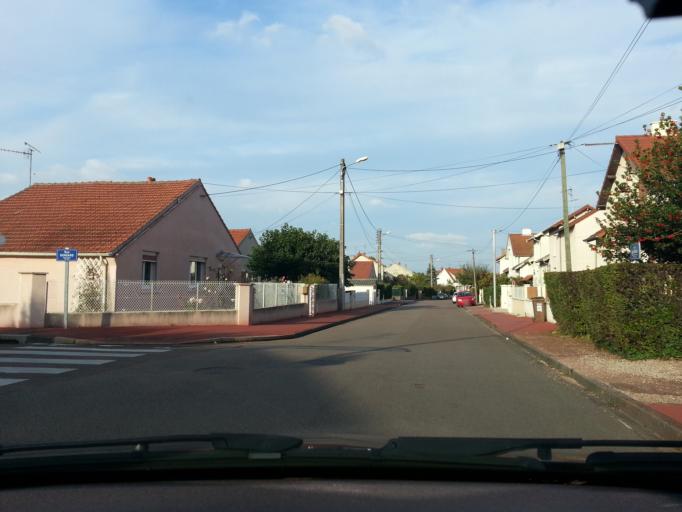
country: FR
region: Bourgogne
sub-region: Departement de Saone-et-Loire
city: Chatenoy-le-Royal
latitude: 46.7783
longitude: 4.8208
